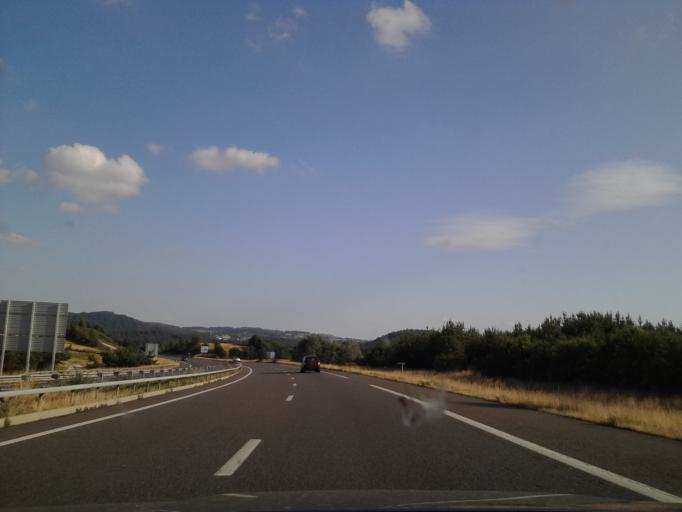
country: FR
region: Languedoc-Roussillon
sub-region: Departement de la Lozere
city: Aumont-Aubrac
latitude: 44.7657
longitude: 3.2830
